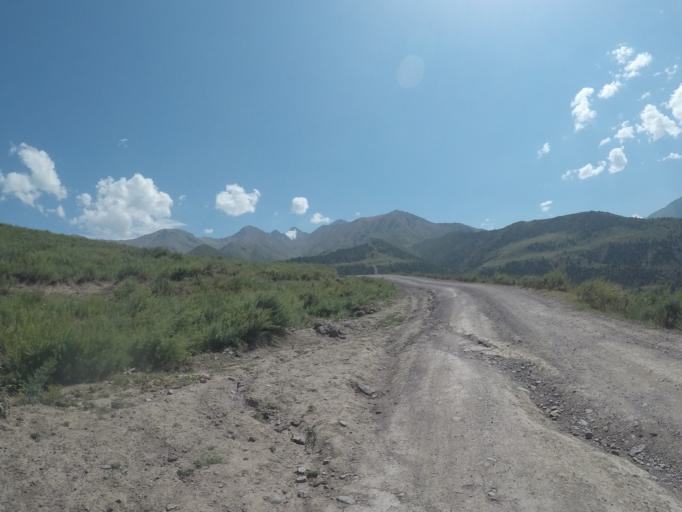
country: KG
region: Chuy
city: Bishkek
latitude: 42.6481
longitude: 74.5215
